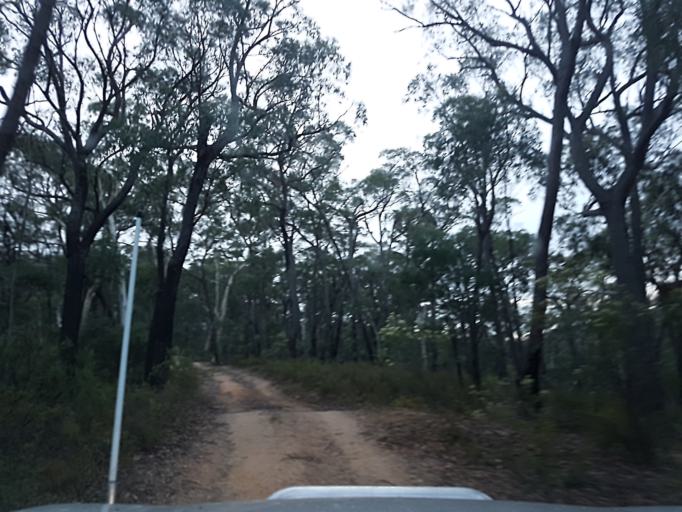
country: AU
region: New South Wales
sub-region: Snowy River
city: Jindabyne
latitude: -36.8636
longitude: 148.2371
